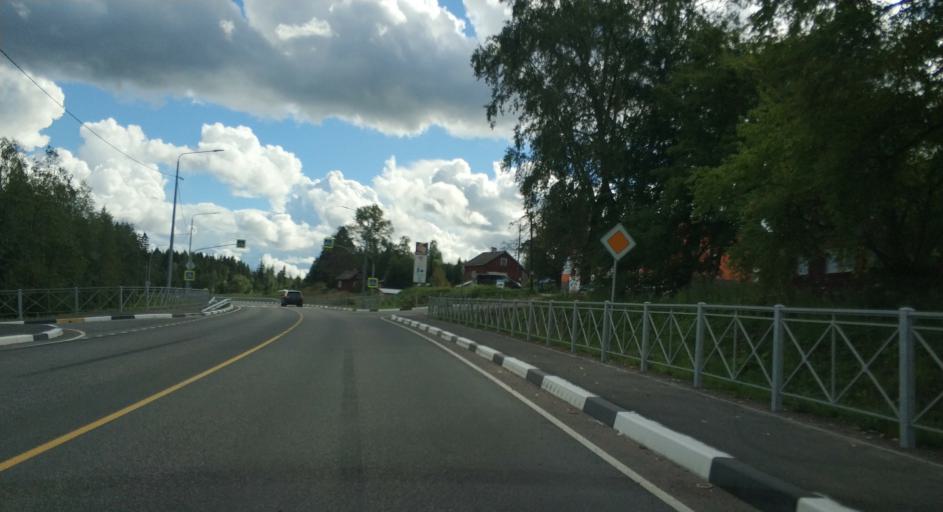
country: RU
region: Republic of Karelia
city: Ruskeala
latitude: 61.9326
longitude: 30.5930
